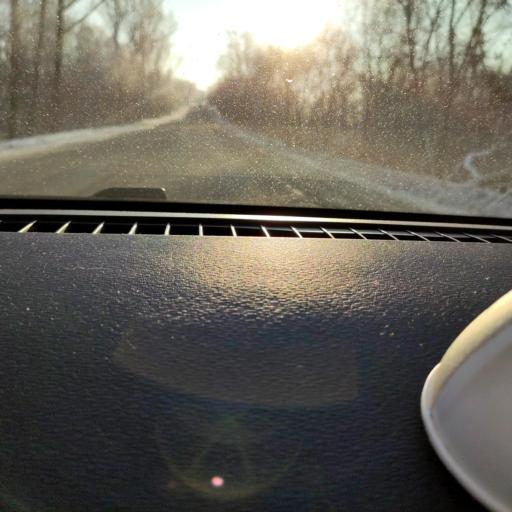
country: RU
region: Samara
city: Samara
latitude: 53.1207
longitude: 50.2322
